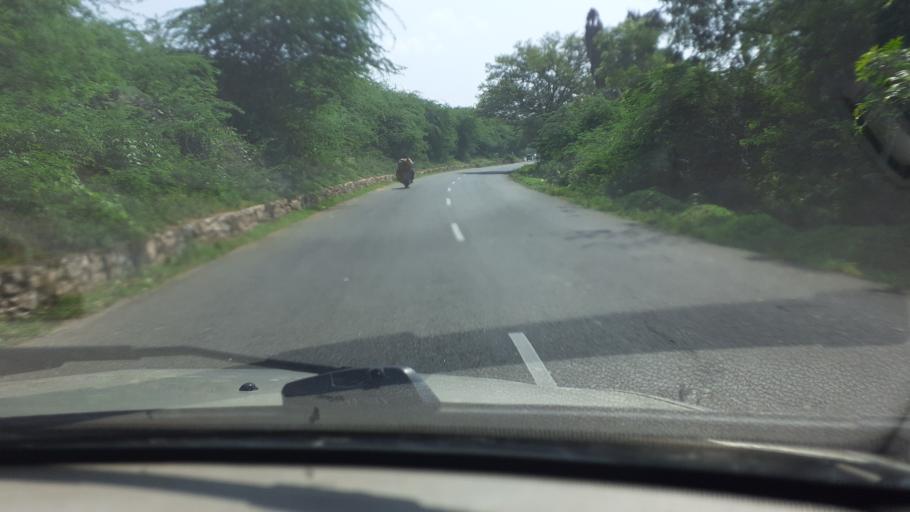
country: IN
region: Tamil Nadu
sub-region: Thoothukkudi
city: Srivaikuntam
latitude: 8.6142
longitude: 77.9205
